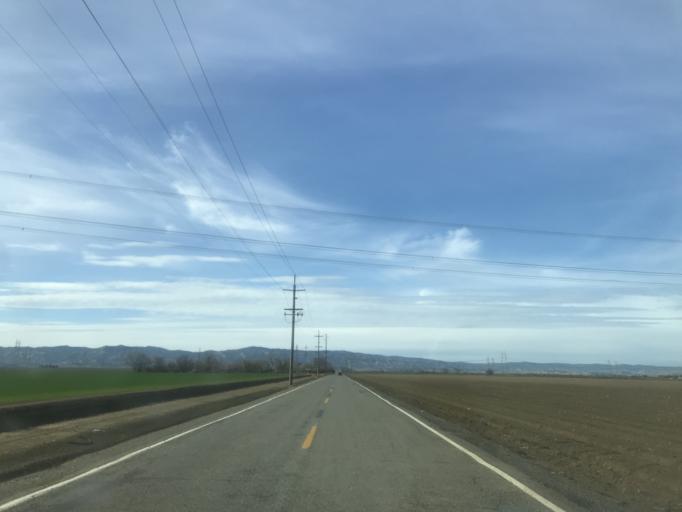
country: US
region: California
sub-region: Yolo County
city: Cottonwood
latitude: 38.6638
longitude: -121.9341
